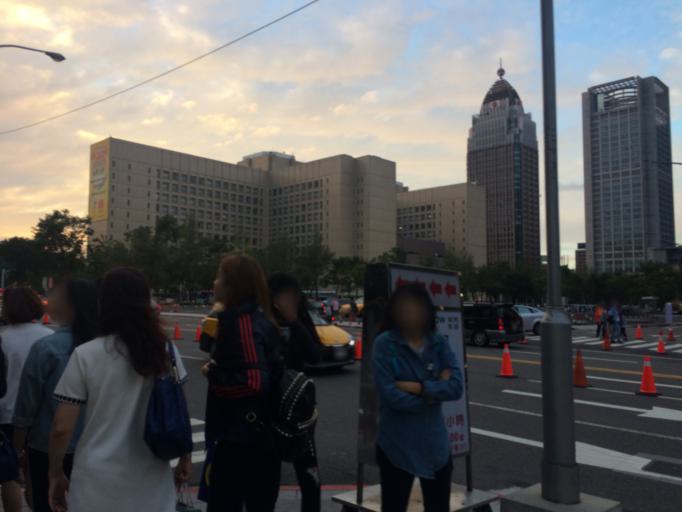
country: TW
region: Taipei
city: Taipei
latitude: 25.0357
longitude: 121.5666
